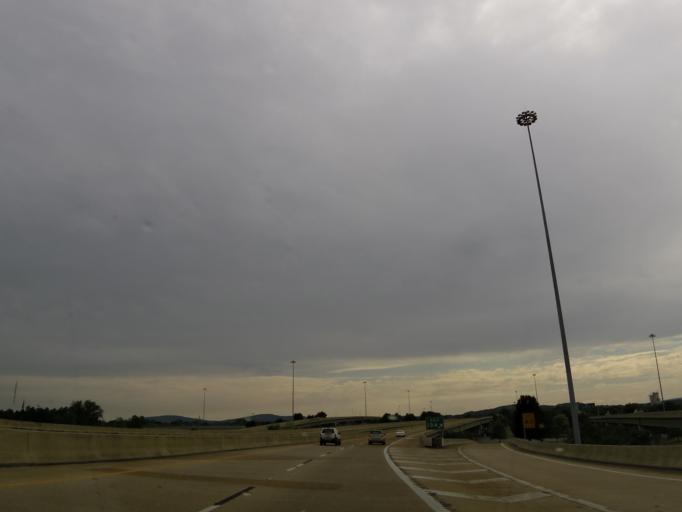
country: US
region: Alabama
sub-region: Madison County
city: Huntsville
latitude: 34.7392
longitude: -86.5867
